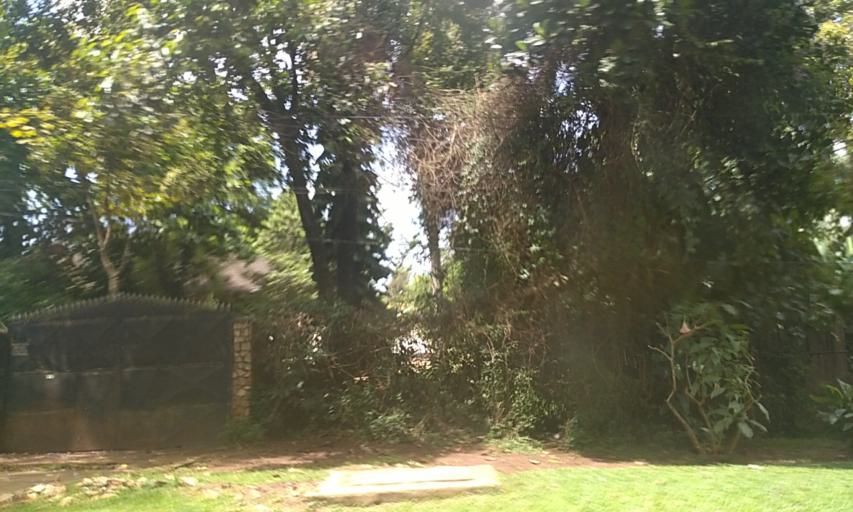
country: UG
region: Central Region
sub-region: Kampala District
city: Kampala
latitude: 0.3276
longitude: 32.6025
